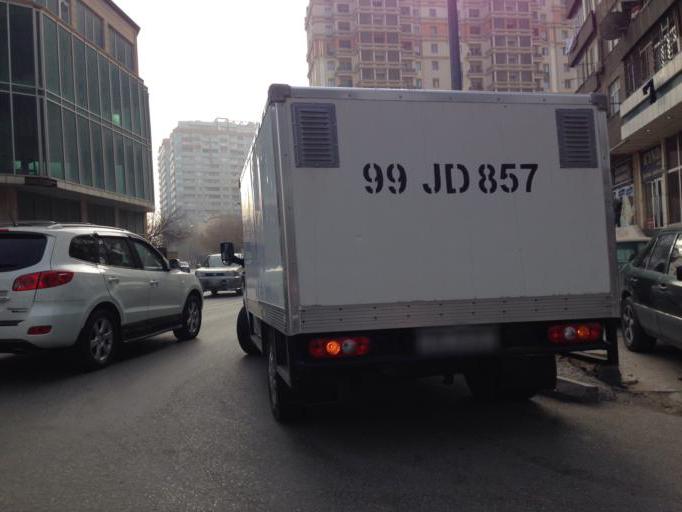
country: AZ
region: Baki
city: Baku
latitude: 40.4020
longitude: 49.8632
